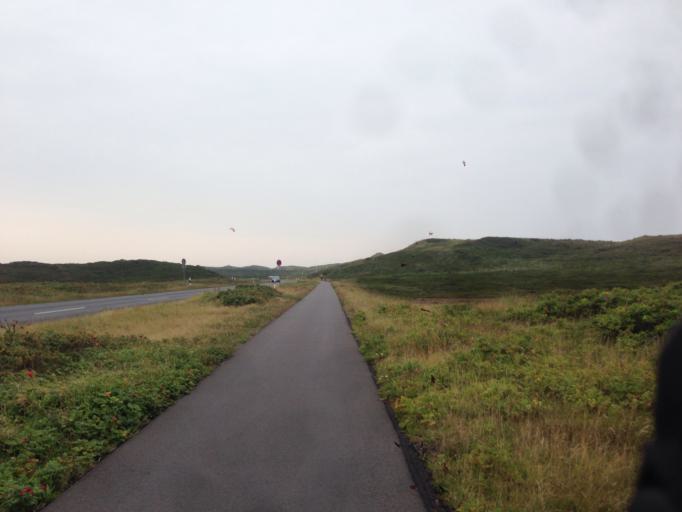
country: DE
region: Schleswig-Holstein
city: Norddorf
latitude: 54.7806
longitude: 8.2853
